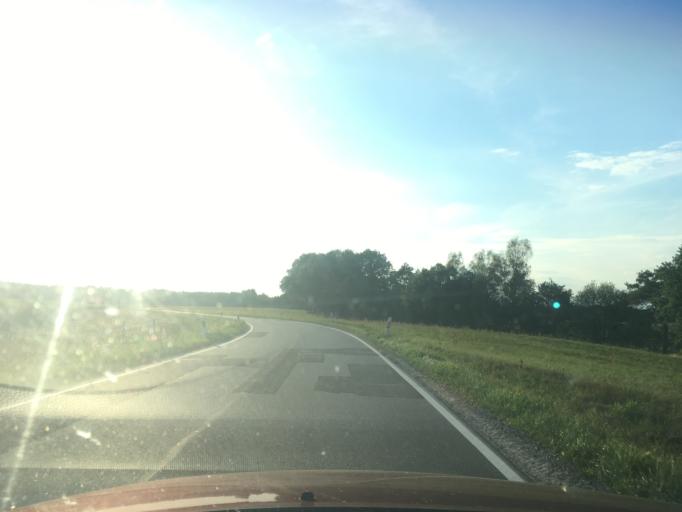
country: DE
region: Saxony
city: Rothenburg
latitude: 51.3166
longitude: 14.9893
